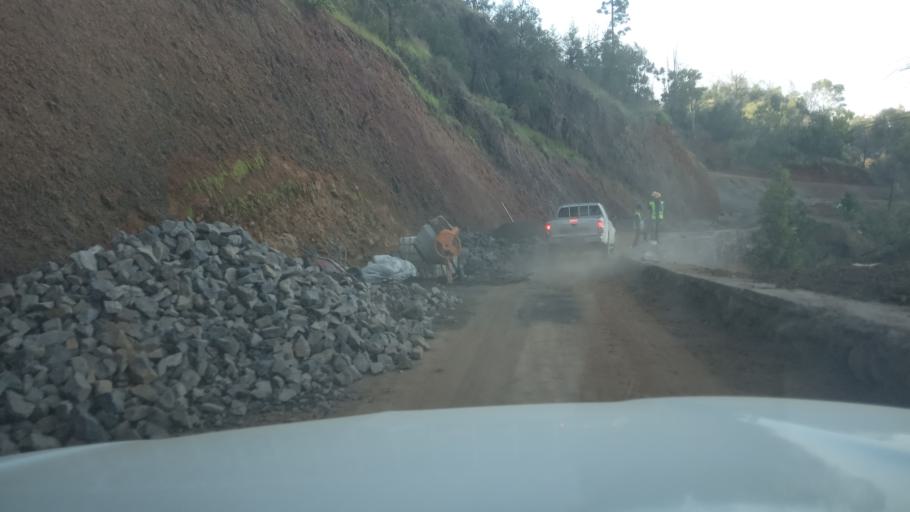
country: CV
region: Mosteiros
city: Porto dos Mosteiros
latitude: 14.9985
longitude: -24.3451
